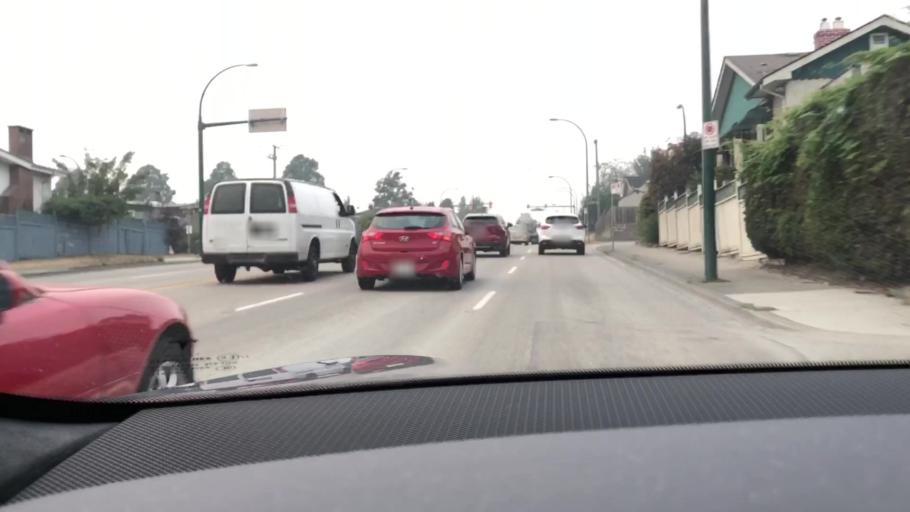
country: CA
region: British Columbia
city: Vancouver
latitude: 49.2148
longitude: -123.0770
